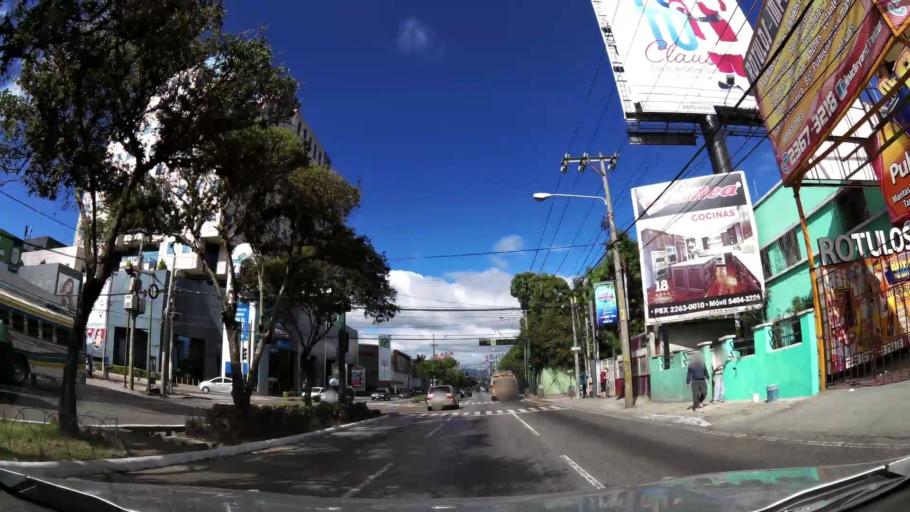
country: GT
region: Guatemala
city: Santa Catarina Pinula
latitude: 14.5925
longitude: -90.5116
